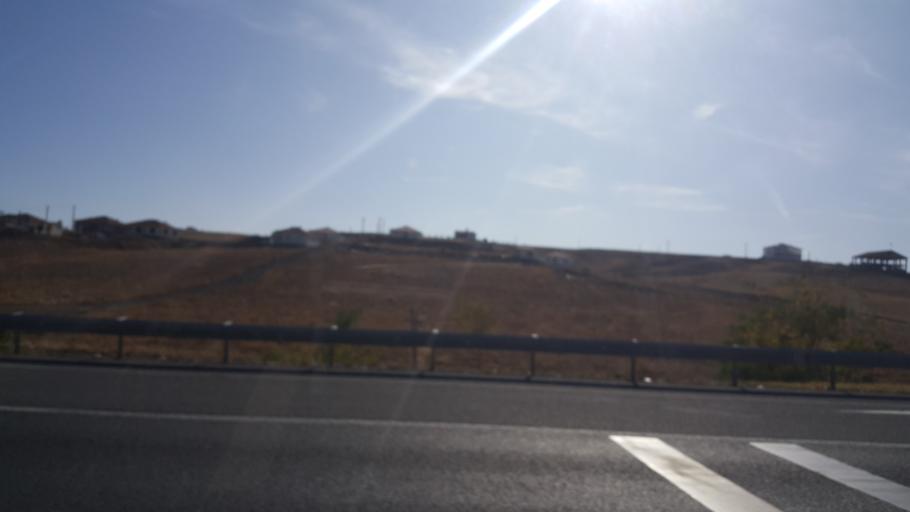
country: TR
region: Konya
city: Kulu
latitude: 39.2712
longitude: 32.9654
